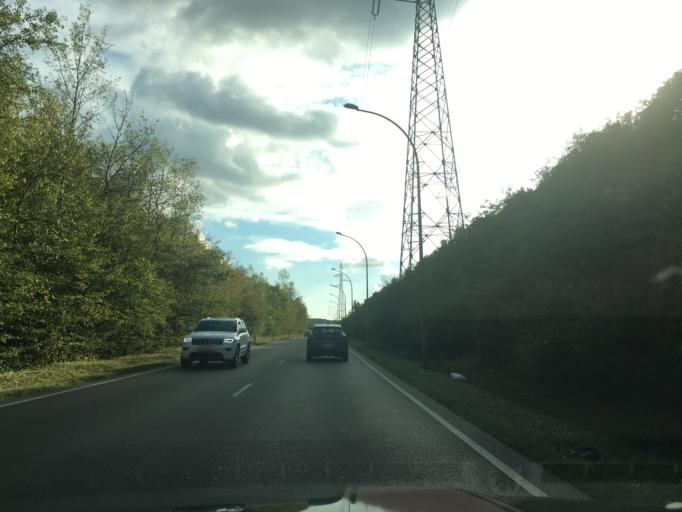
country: LU
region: Luxembourg
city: Soleuvre
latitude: 49.5279
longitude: 5.9255
